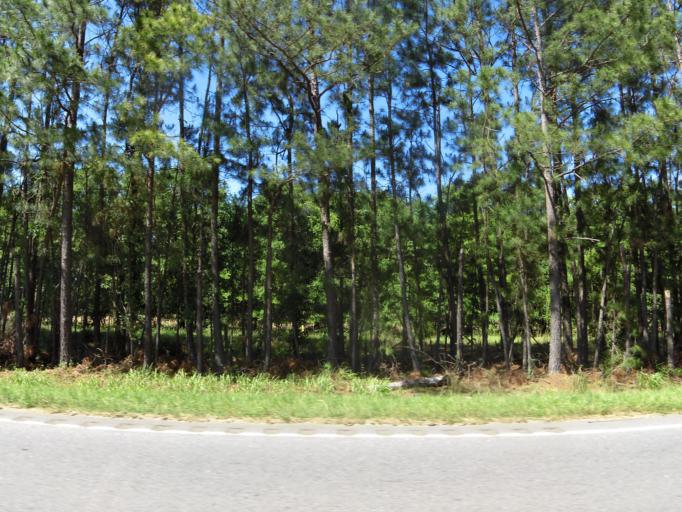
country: US
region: South Carolina
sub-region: Aiken County
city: Aiken
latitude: 33.5408
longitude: -81.6643
